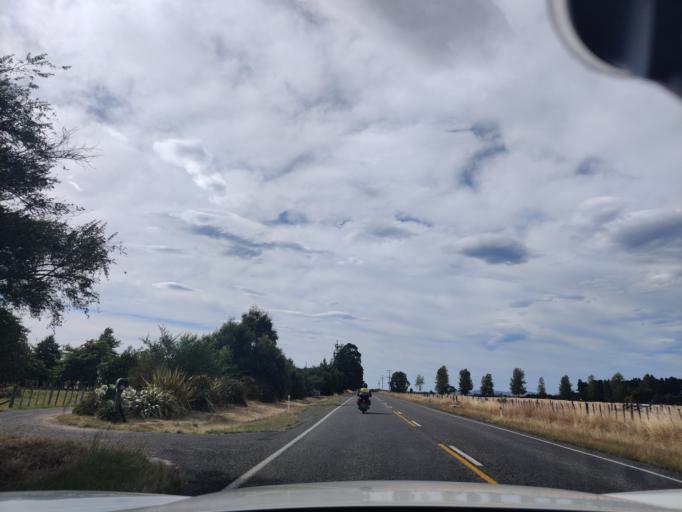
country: NZ
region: Wellington
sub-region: Masterton District
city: Masterton
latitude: -40.8731
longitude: 175.6506
